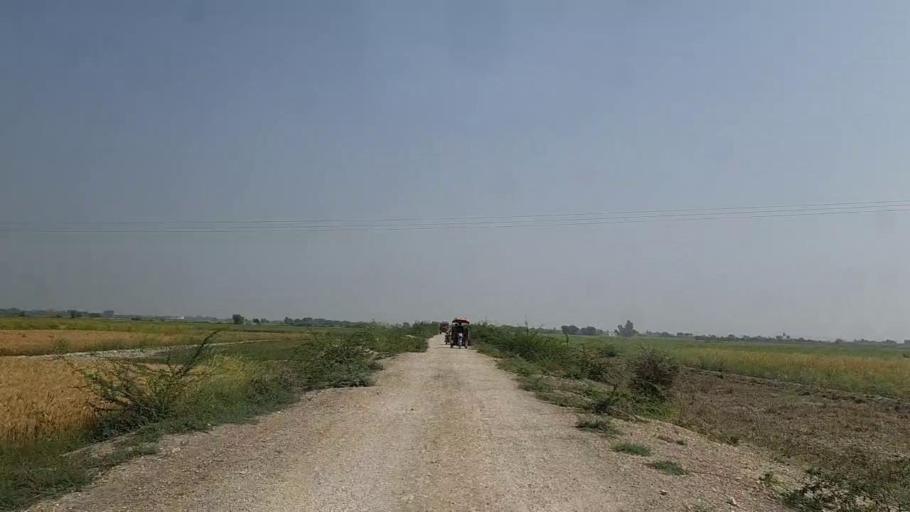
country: PK
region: Sindh
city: Naukot
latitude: 24.8097
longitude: 69.3716
